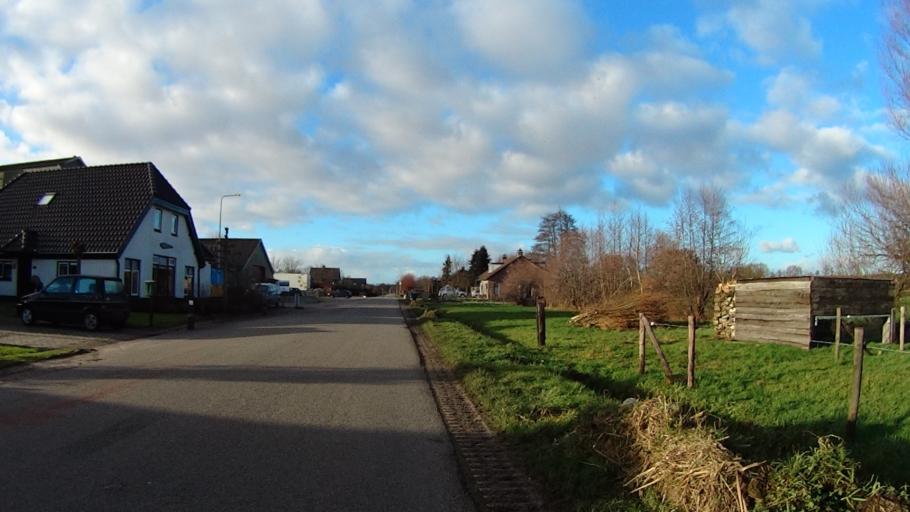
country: NL
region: Gelderland
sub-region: Gemeente Barneveld
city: Zwartebroek
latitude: 52.1831
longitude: 5.4993
